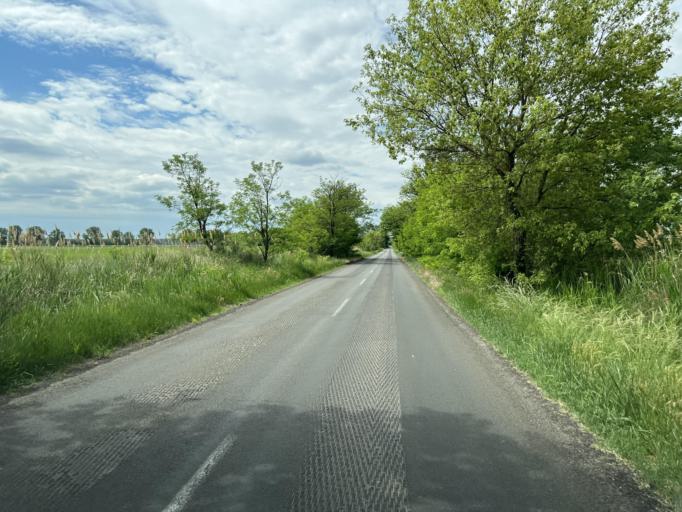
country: HU
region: Pest
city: Szentlorinckata
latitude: 47.4911
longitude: 19.7370
